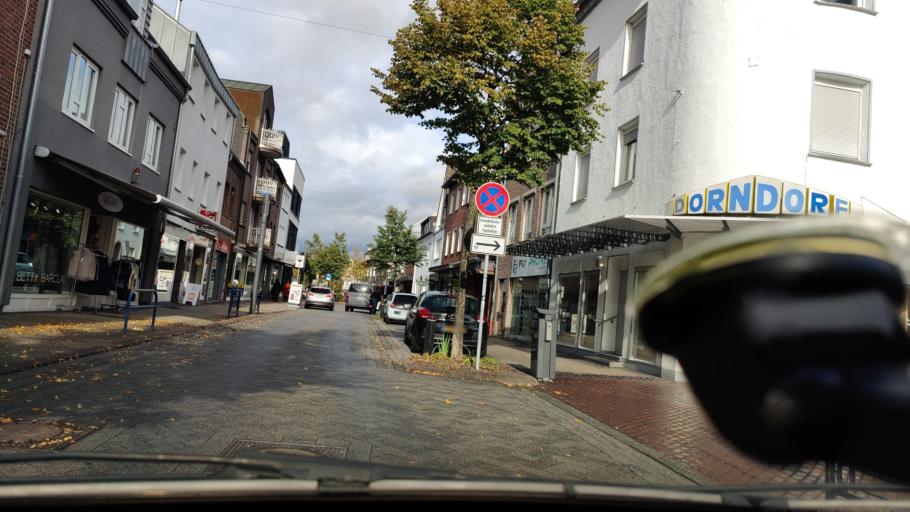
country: DE
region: North Rhine-Westphalia
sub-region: Regierungsbezirk Koln
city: Heinsberg
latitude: 51.0639
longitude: 6.0961
